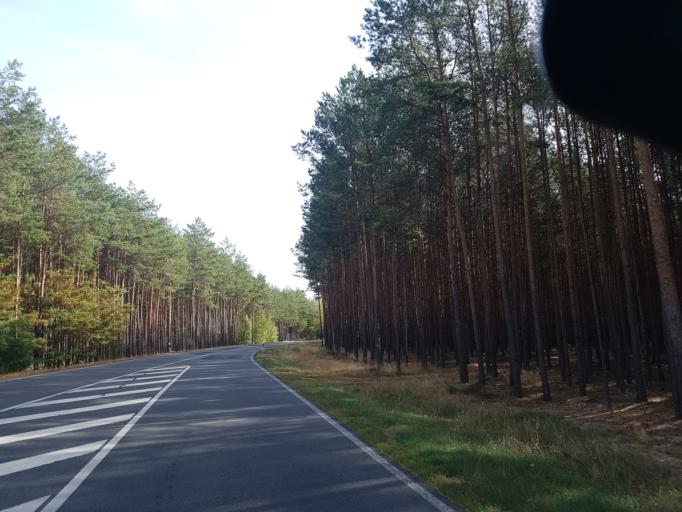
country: DE
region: Brandenburg
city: Schlieben
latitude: 51.6933
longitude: 13.4313
